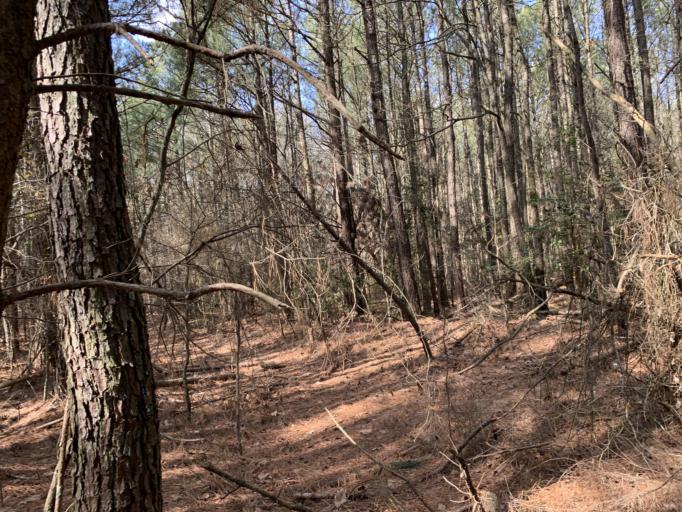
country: US
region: Delaware
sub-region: Sussex County
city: Georgetown
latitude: 38.6806
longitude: -75.4773
